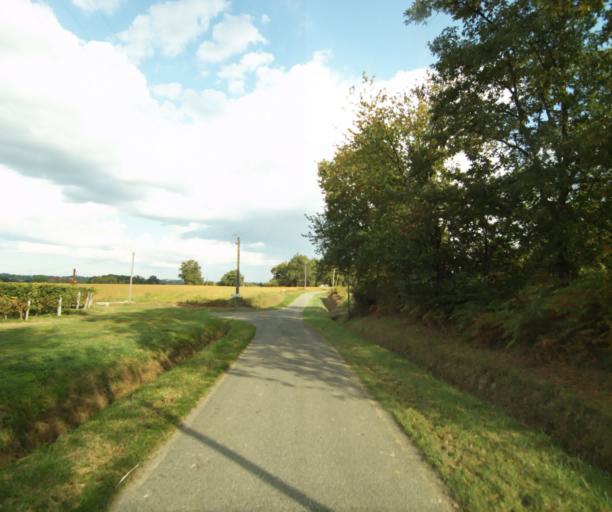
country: FR
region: Midi-Pyrenees
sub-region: Departement du Gers
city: Cazaubon
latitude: 43.9009
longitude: -0.0708
